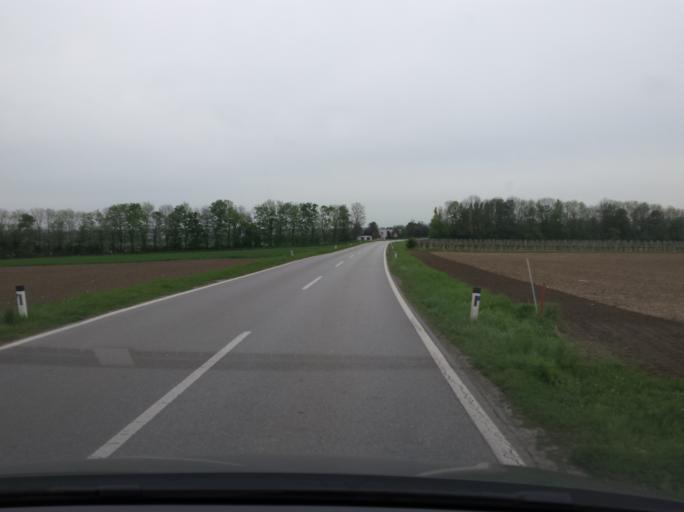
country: AT
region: Lower Austria
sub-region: Politischer Bezirk Bruck an der Leitha
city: Bruck an der Leitha
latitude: 48.0383
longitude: 16.7566
